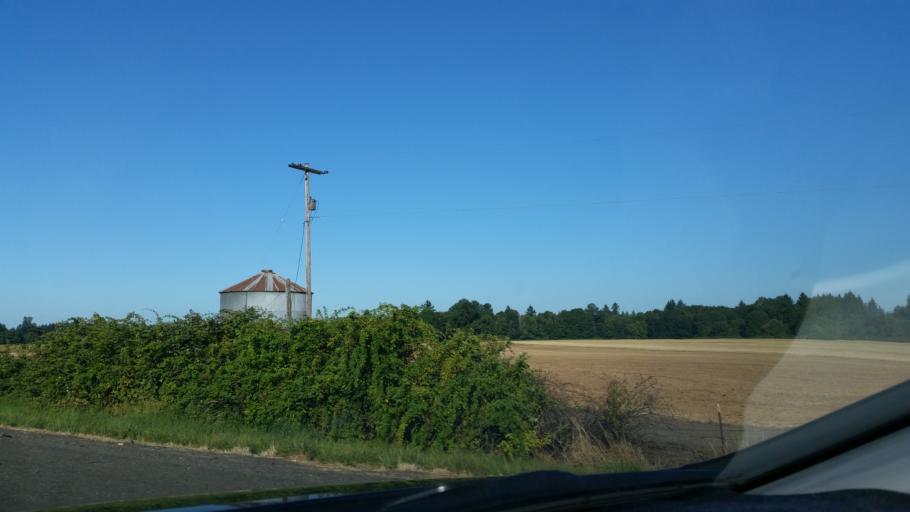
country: US
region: Oregon
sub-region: Marion County
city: Hubbard
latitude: 45.2395
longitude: -122.8027
